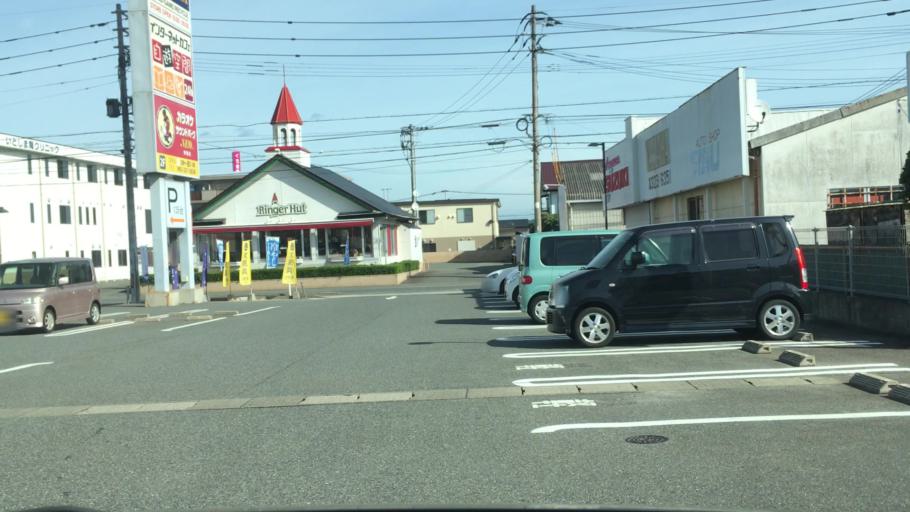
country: JP
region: Fukuoka
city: Maebaru-chuo
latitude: 33.5704
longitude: 130.2370
